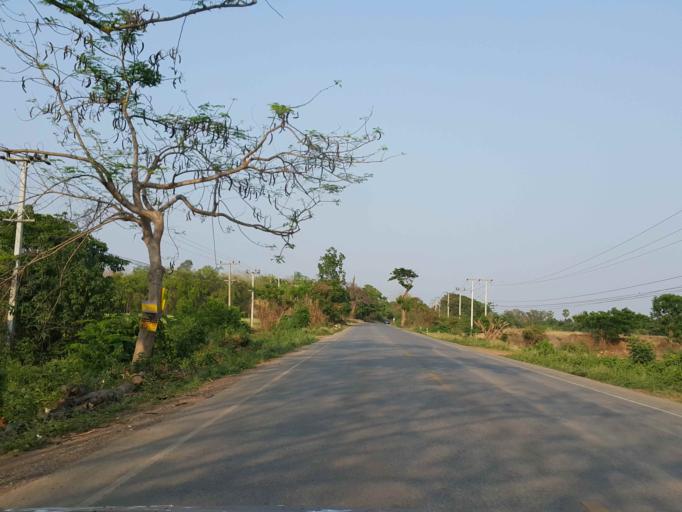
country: TH
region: Sukhothai
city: Sawankhalok
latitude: 17.3083
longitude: 99.7867
